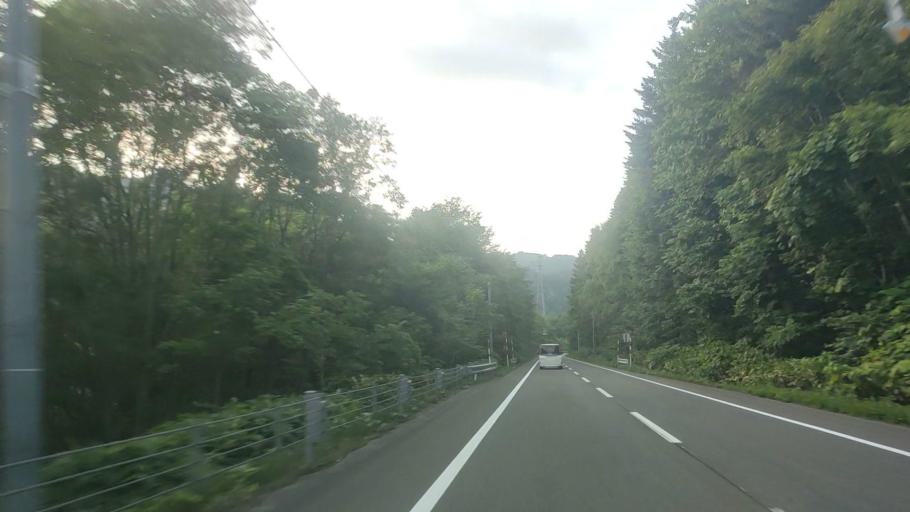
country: JP
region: Hokkaido
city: Ashibetsu
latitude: 43.3440
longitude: 142.1521
